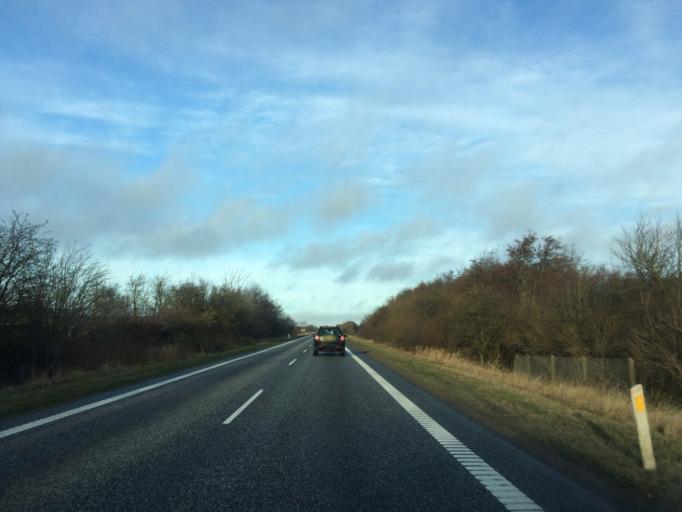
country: DK
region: North Denmark
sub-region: Thisted Kommune
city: Thisted
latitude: 56.8905
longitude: 8.5974
